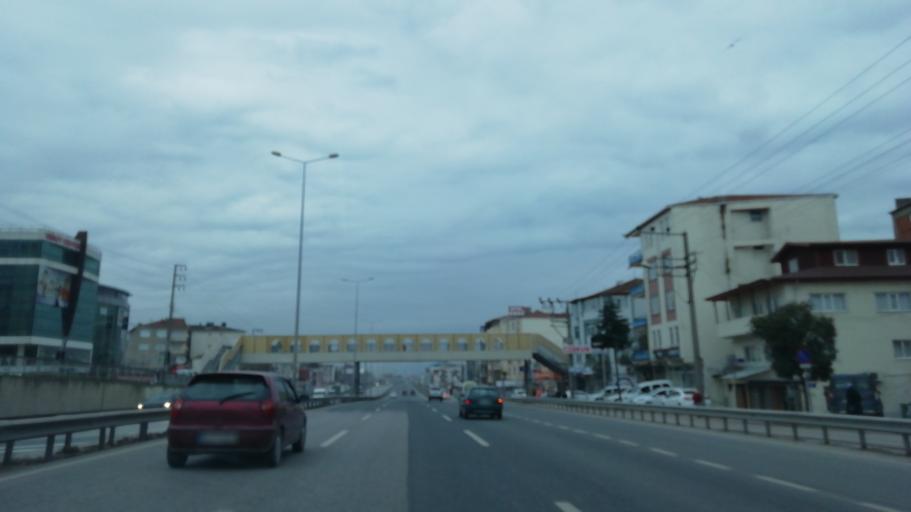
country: TR
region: Kocaeli
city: Korfez
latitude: 40.7635
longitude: 29.7808
